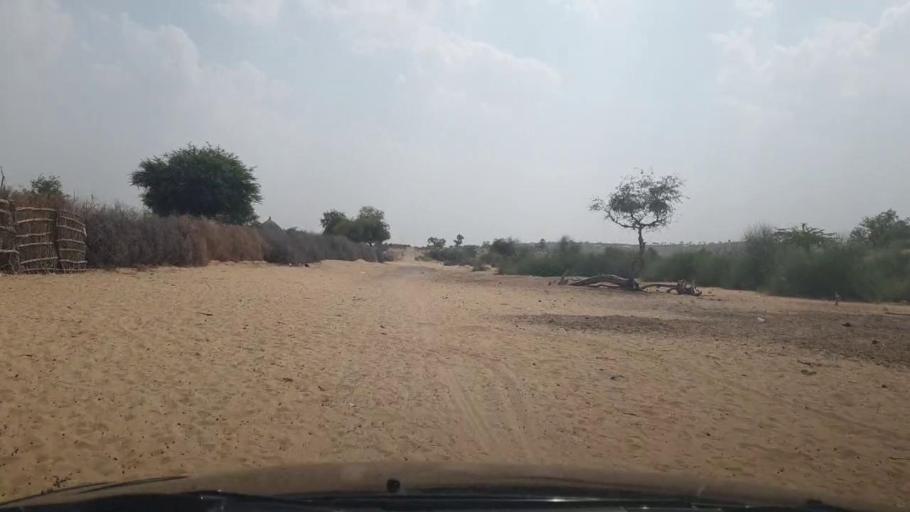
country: PK
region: Sindh
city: Islamkot
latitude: 25.0110
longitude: 70.5270
